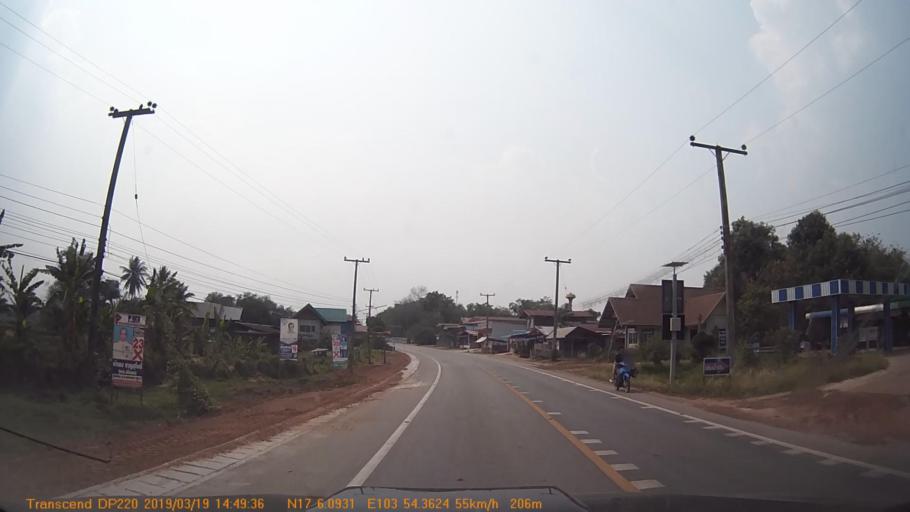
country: TH
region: Sakon Nakhon
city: Kut Bak
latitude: 17.1016
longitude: 103.9059
